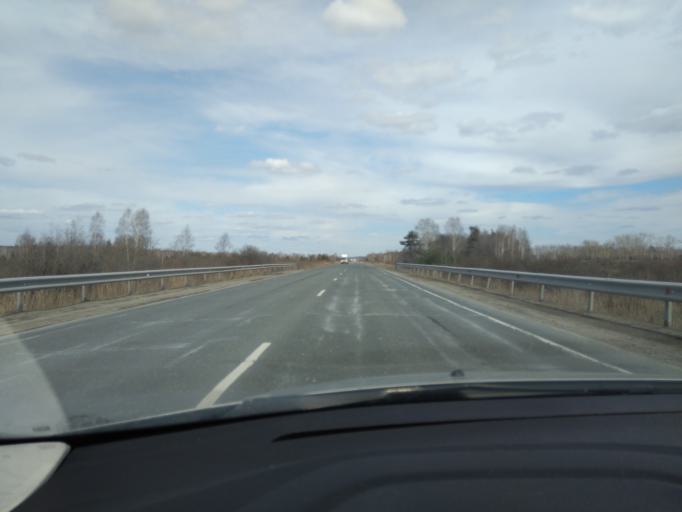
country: RU
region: Sverdlovsk
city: Yelanskiy
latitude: 56.8189
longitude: 62.5445
